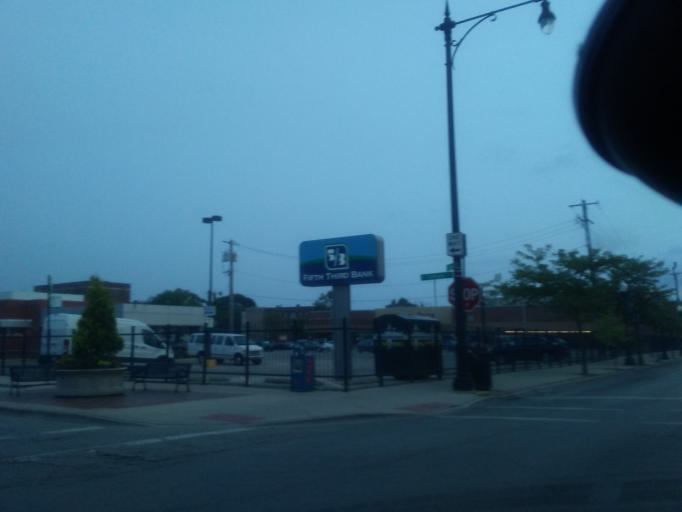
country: US
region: Illinois
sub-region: Cook County
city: Evanston
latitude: 41.9817
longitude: -87.6684
